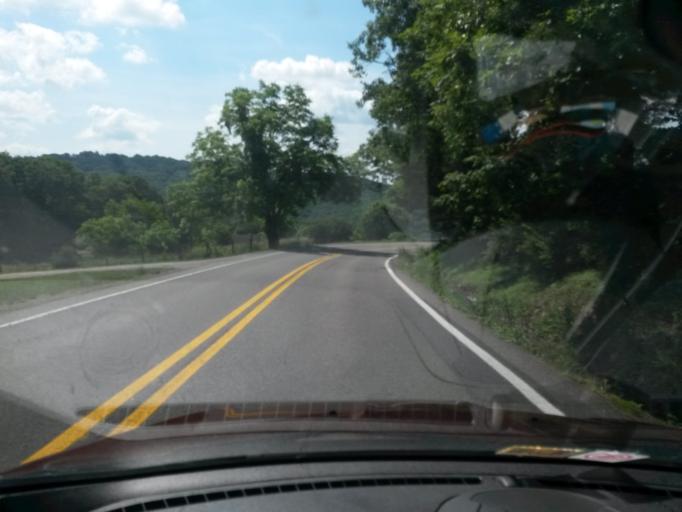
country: US
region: West Virginia
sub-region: Mercer County
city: Princeton
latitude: 37.3918
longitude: -81.1179
